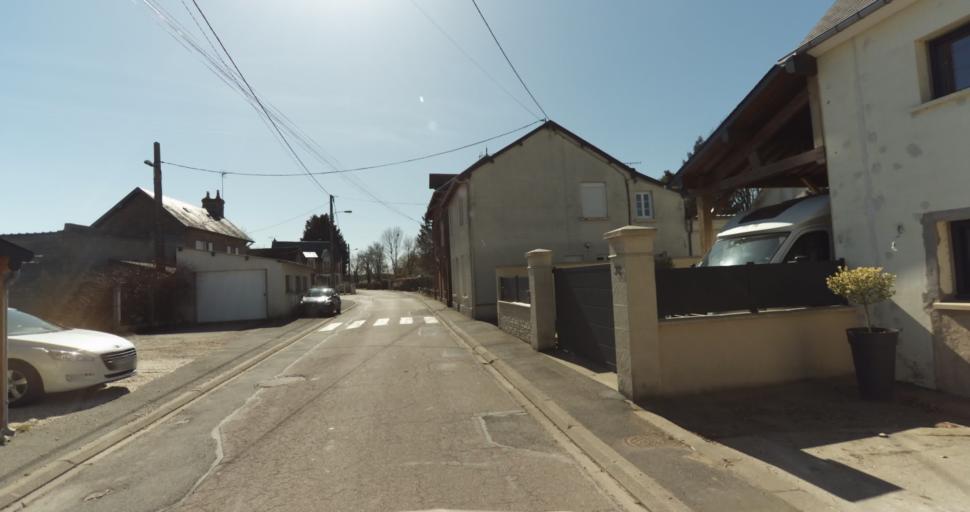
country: FR
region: Lower Normandy
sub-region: Departement du Calvados
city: Livarot
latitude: 48.9673
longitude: 0.0750
